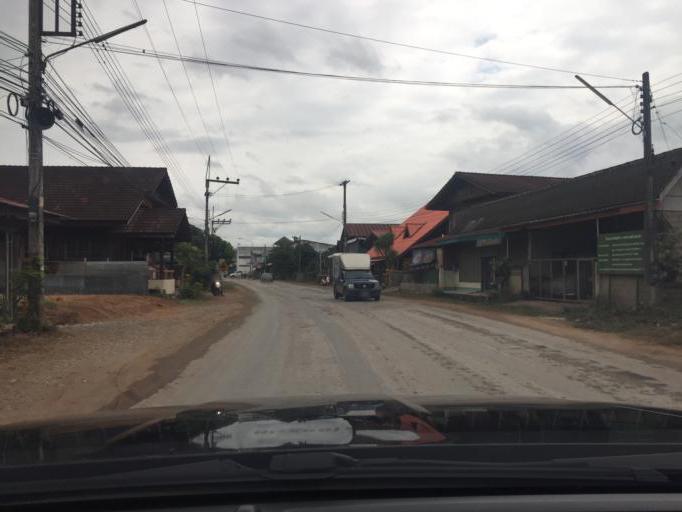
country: TH
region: Phayao
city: Pong
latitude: 19.1672
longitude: 100.2866
